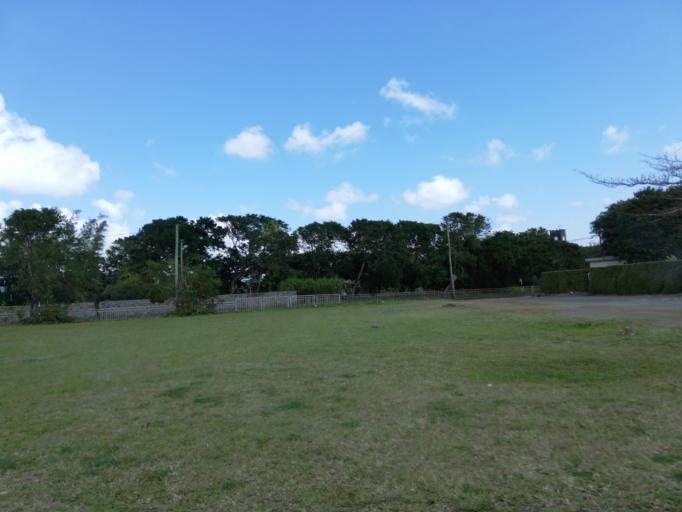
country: MU
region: Moka
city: Verdun
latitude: -20.2209
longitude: 57.5383
